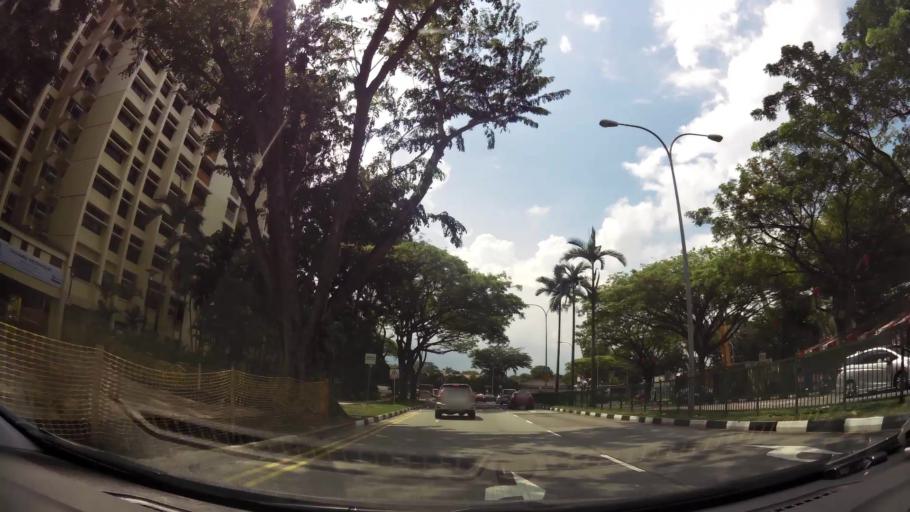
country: MY
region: Johor
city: Kampung Pasir Gudang Baru
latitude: 1.4302
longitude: 103.8276
